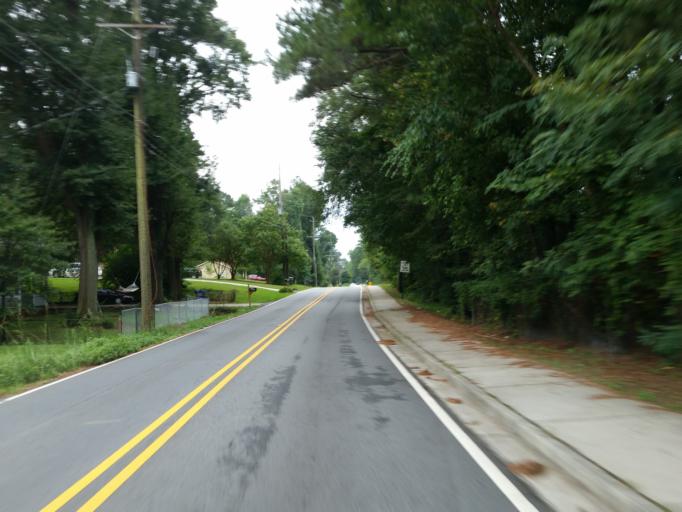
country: US
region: Georgia
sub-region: Cobb County
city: Austell
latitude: 33.8315
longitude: -84.6232
